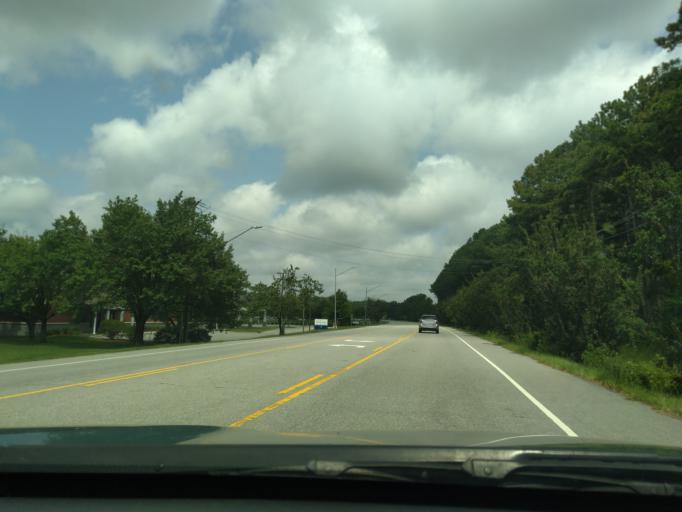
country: US
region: North Carolina
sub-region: Edgecombe County
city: Tarboro
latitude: 35.9222
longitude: -77.5648
